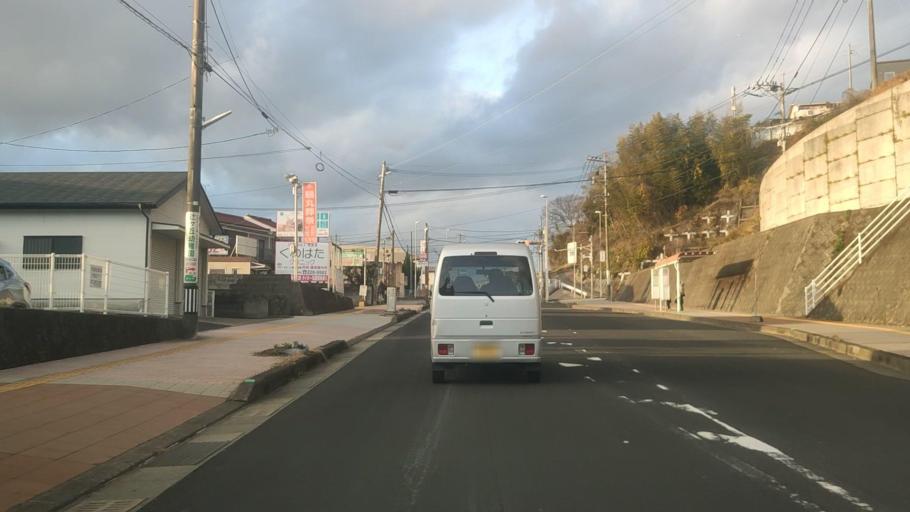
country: JP
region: Kagoshima
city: Kagoshima-shi
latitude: 31.6197
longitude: 130.5534
